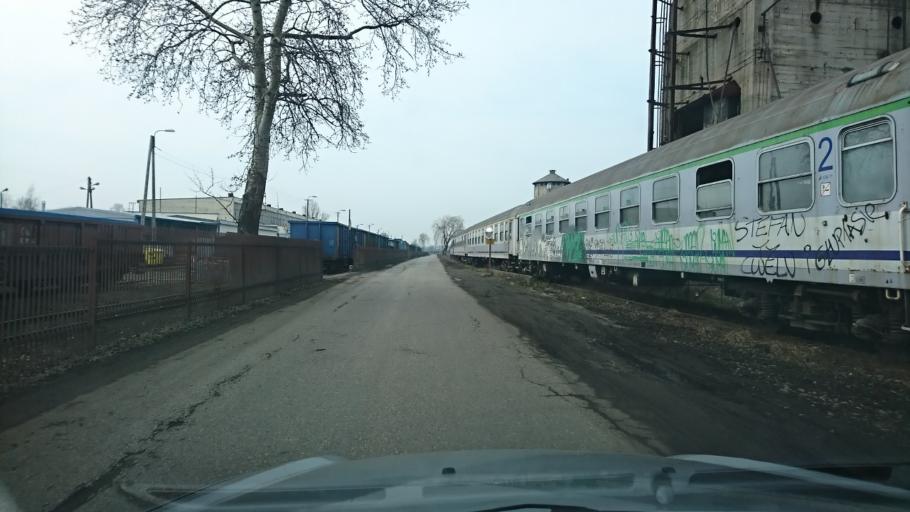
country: PL
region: Lesser Poland Voivodeship
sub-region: Powiat wielicki
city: Czarnochowice
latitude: 50.0242
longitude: 20.0245
